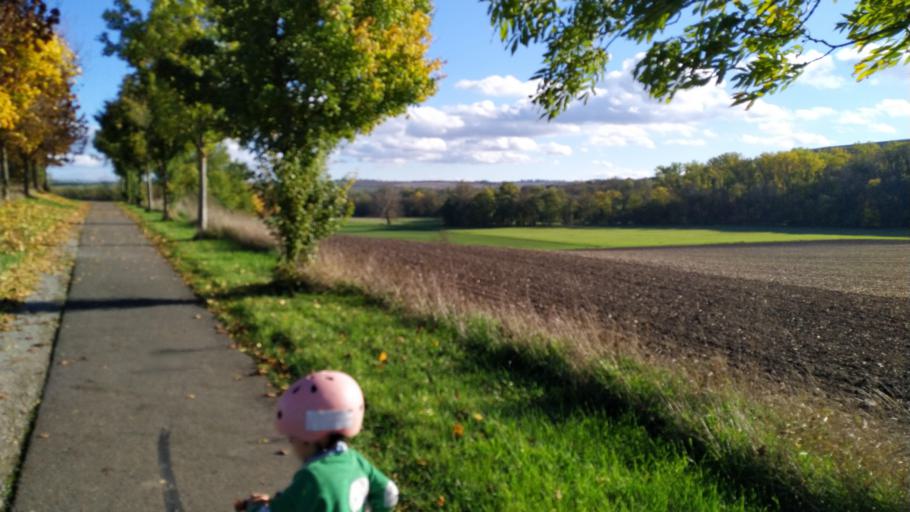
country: DE
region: Thuringia
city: Mattstedt
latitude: 51.0545
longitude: 11.5241
